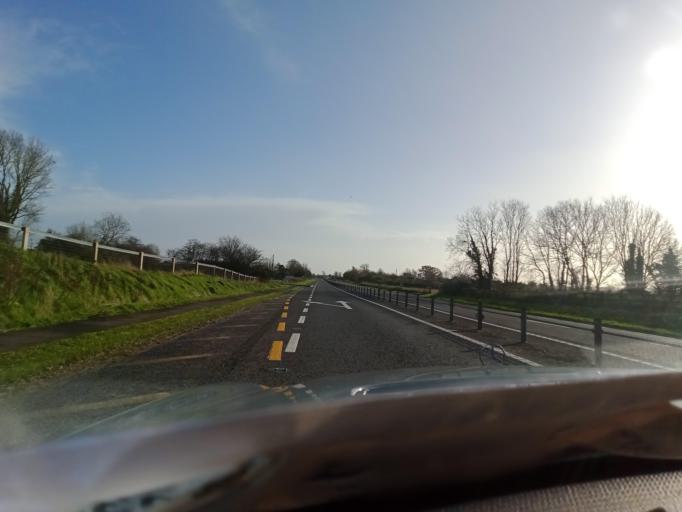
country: IE
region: Munster
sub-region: Waterford
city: Portlaw
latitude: 52.3146
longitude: -7.2883
